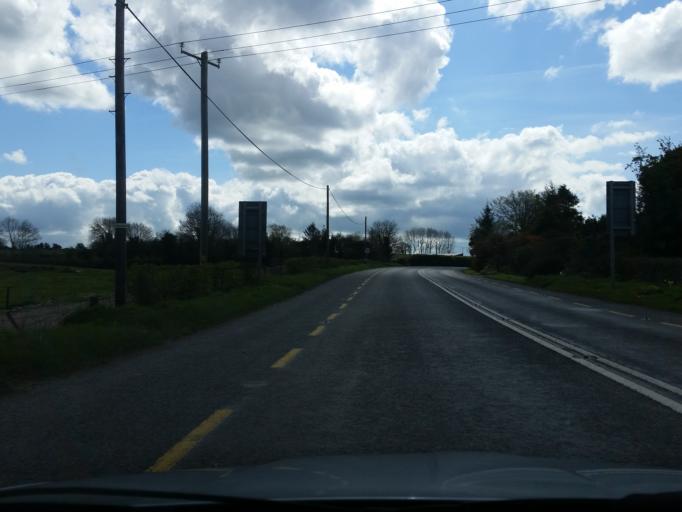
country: IE
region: Leinster
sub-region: An Mhi
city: Slane
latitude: 53.6952
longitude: -6.5389
